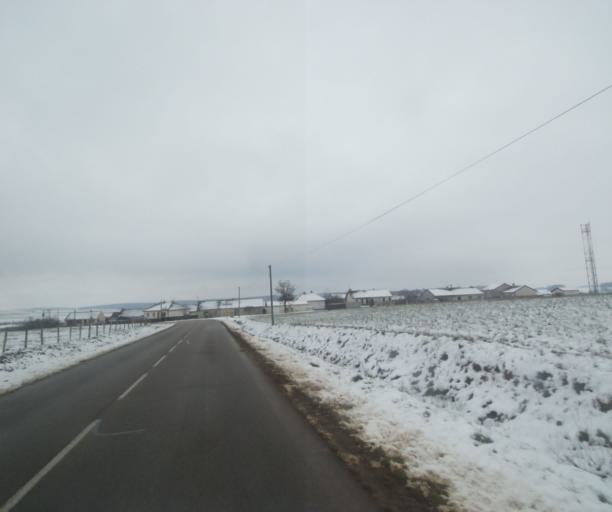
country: FR
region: Champagne-Ardenne
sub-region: Departement de la Haute-Marne
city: Laneuville-a-Remy
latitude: 48.4212
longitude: 4.8389
